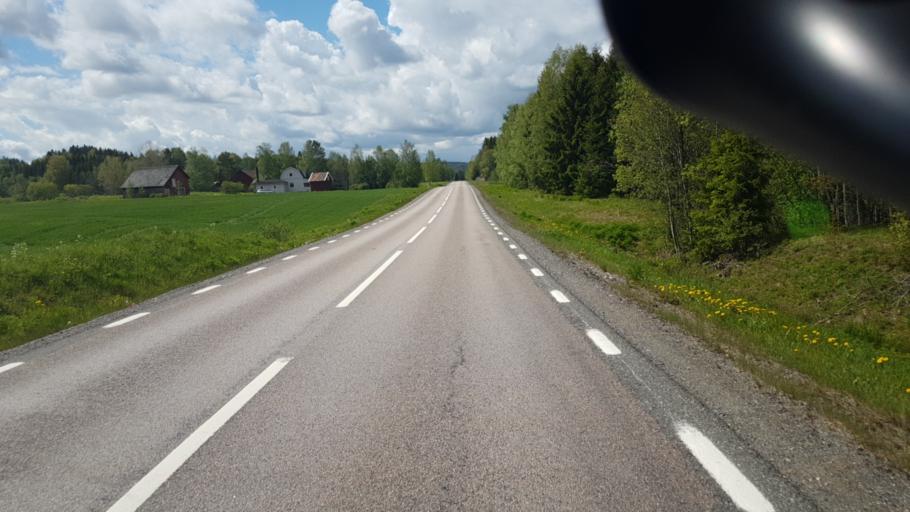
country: SE
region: Vaermland
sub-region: Arjangs Kommun
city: Arjaeng
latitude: 59.5980
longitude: 12.1458
